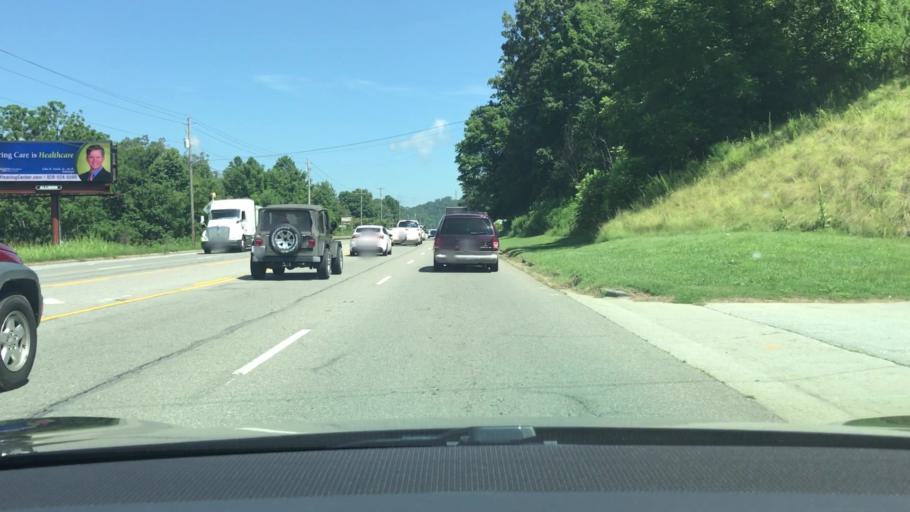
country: US
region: North Carolina
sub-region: Macon County
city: Franklin
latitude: 35.1220
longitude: -83.3930
